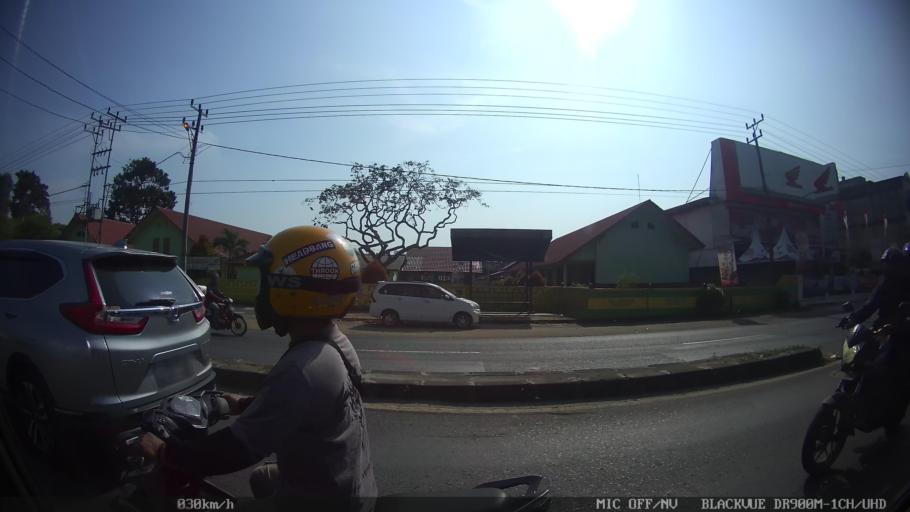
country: ID
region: Lampung
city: Natar
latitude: -5.3080
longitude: 105.1930
